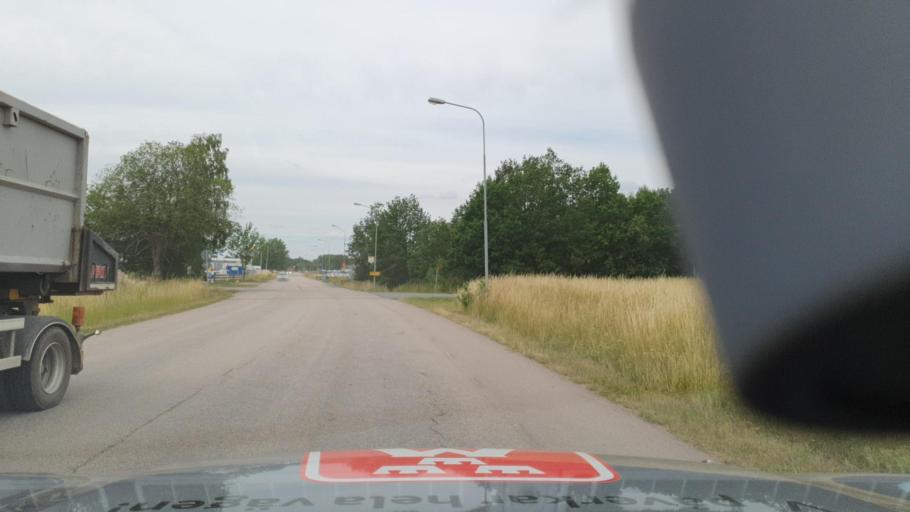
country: SE
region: Kalmar
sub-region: Kalmar Kommun
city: Rinkabyholm
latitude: 56.6756
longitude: 16.2621
